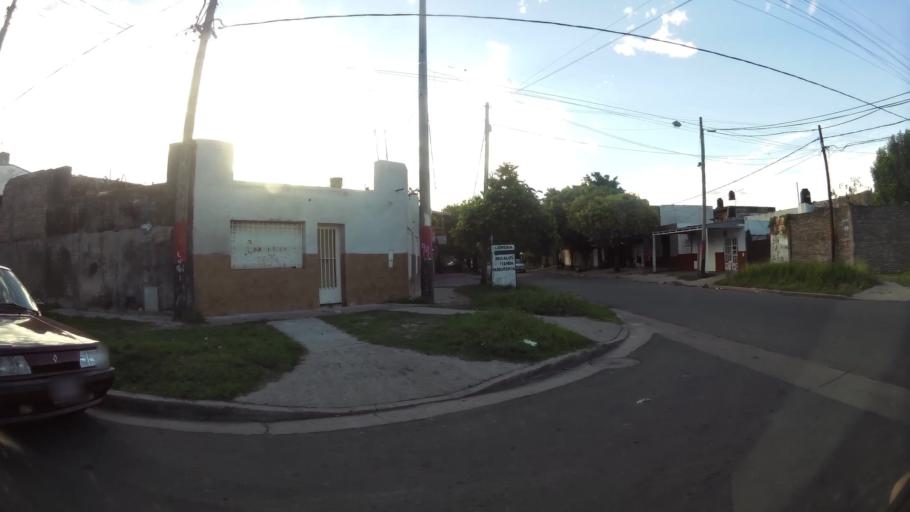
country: AR
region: Santa Fe
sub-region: Departamento de Rosario
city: Rosario
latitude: -32.9808
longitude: -60.6641
